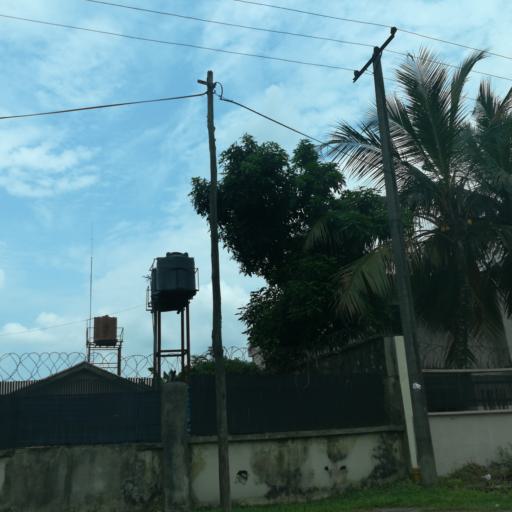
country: NG
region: Rivers
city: Port Harcourt
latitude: 4.8294
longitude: 6.9948
